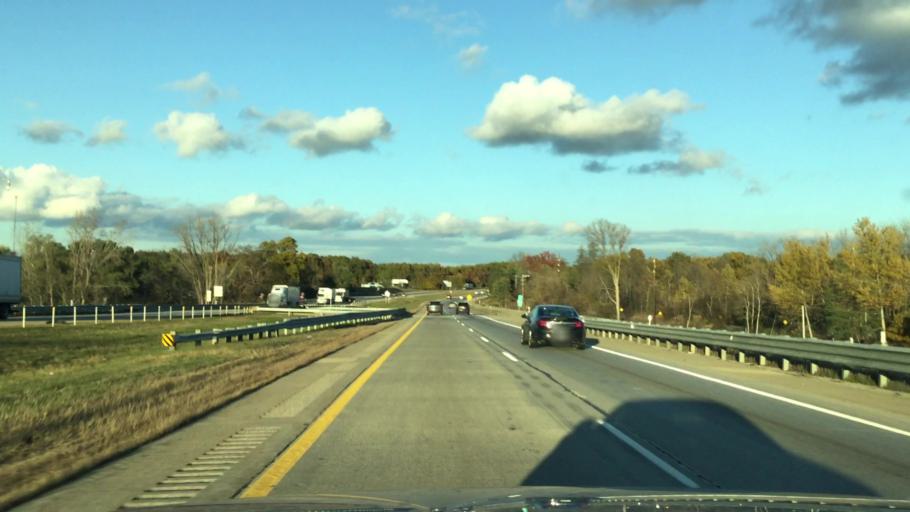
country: US
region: Michigan
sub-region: Calhoun County
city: Brownlee Park
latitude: 42.2809
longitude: -85.1569
